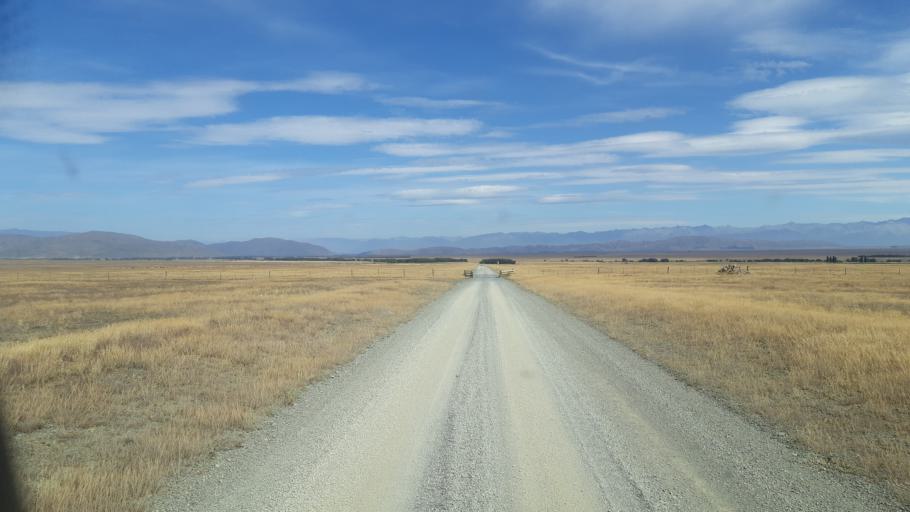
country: NZ
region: Canterbury
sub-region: Timaru District
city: Pleasant Point
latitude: -44.1949
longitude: 170.5411
